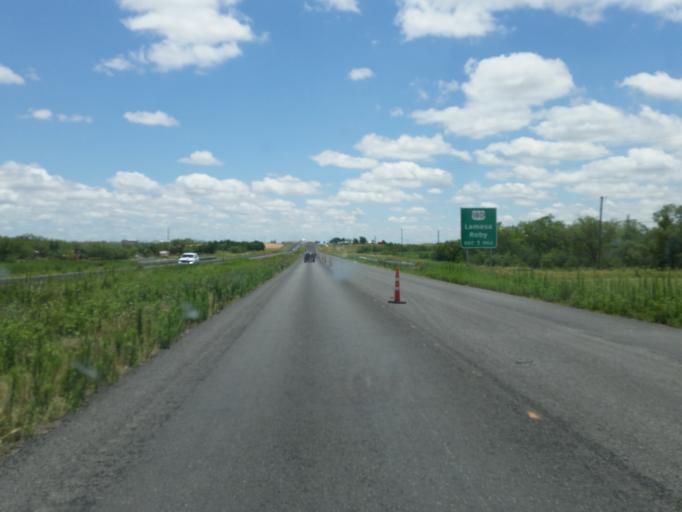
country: US
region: Texas
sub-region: Scurry County
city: Snyder
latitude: 32.7196
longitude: -100.8827
